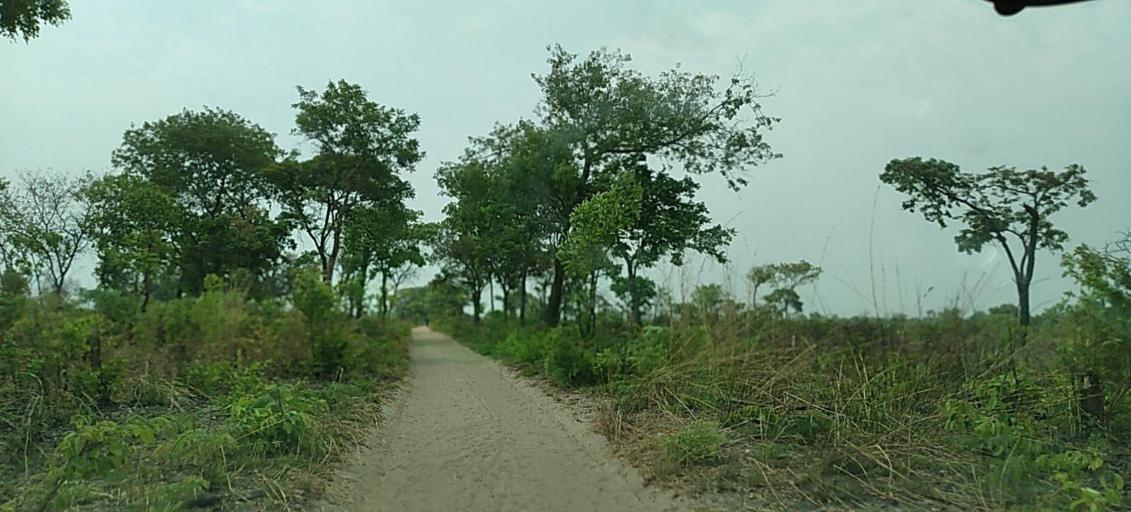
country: ZM
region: North-Western
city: Kabompo
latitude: -13.4705
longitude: 24.4461
